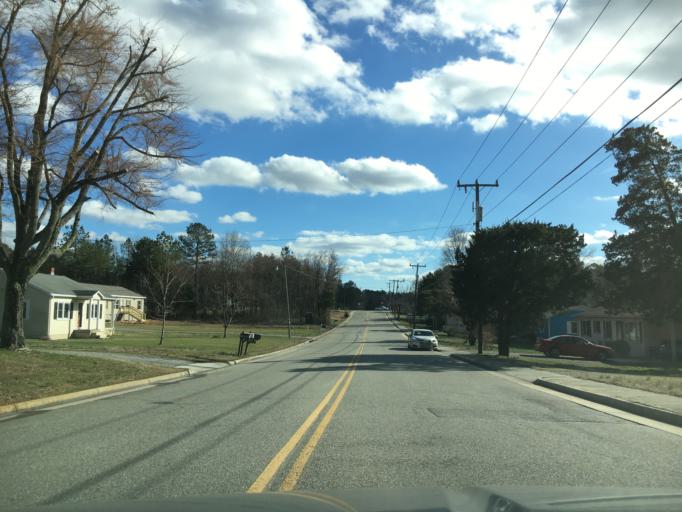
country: US
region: Virginia
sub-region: Halifax County
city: South Boston
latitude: 36.7157
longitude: -78.8887
